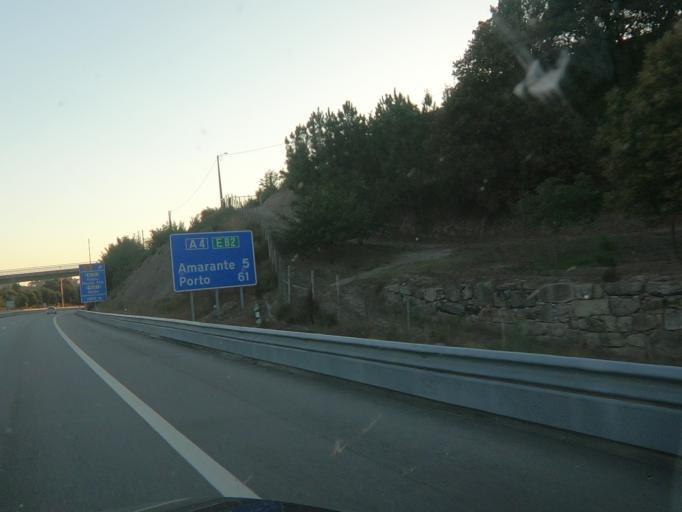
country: PT
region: Porto
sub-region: Amarante
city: Amarante
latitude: 41.2572
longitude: -8.0364
